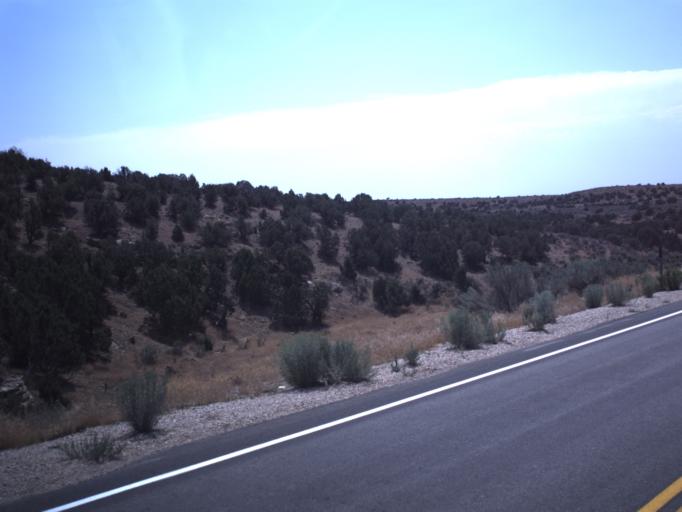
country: US
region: Utah
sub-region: Uintah County
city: Maeser
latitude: 40.4399
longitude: -109.6437
